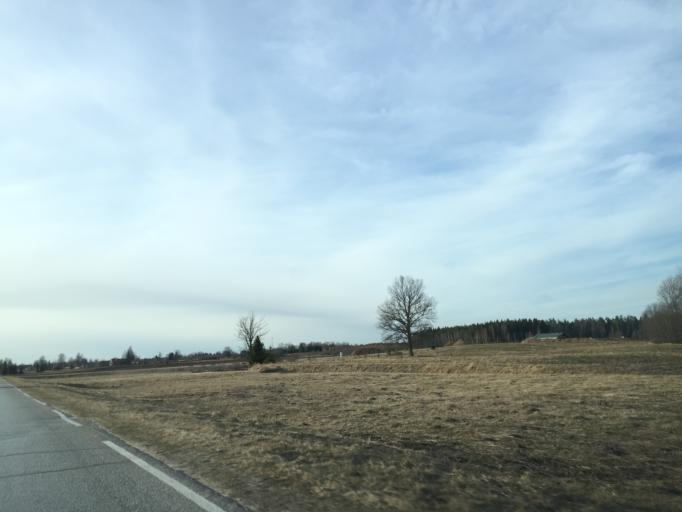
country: LV
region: Krimulda
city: Ragana
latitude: 57.1724
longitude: 24.7295
